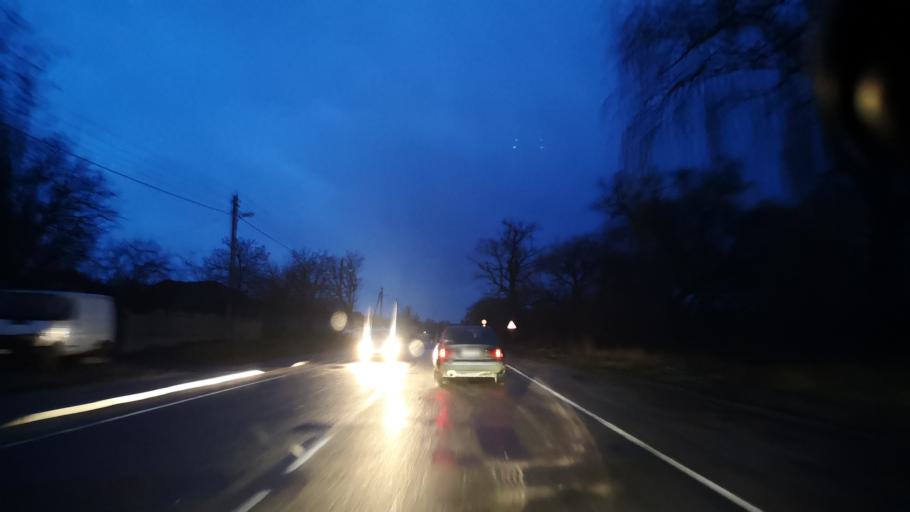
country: MD
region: Orhei
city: Orhei
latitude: 47.4265
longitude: 28.8033
